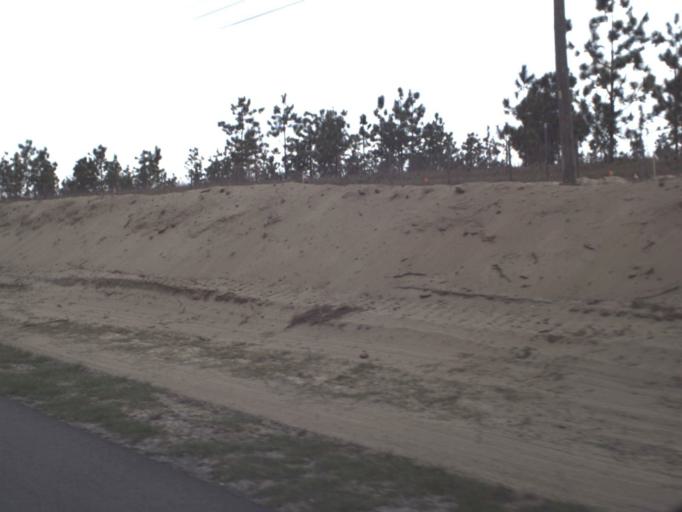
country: US
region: Florida
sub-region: Lake County
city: Clermont
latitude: 28.4408
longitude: -81.7172
